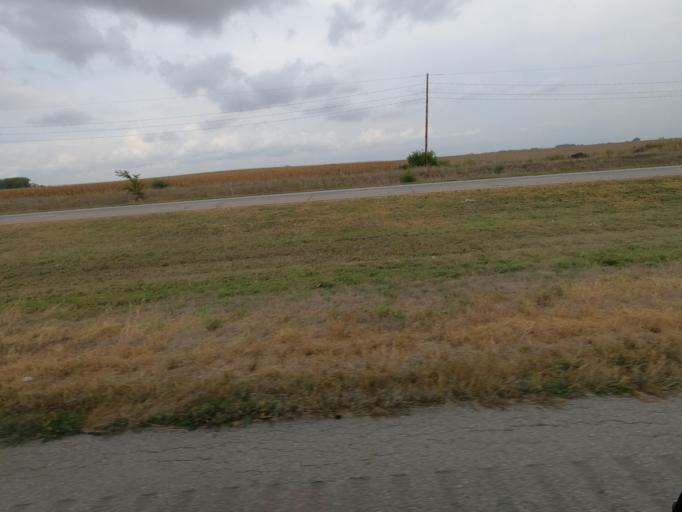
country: US
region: Iowa
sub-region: Jasper County
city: Monroe
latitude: 41.5603
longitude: -93.1506
